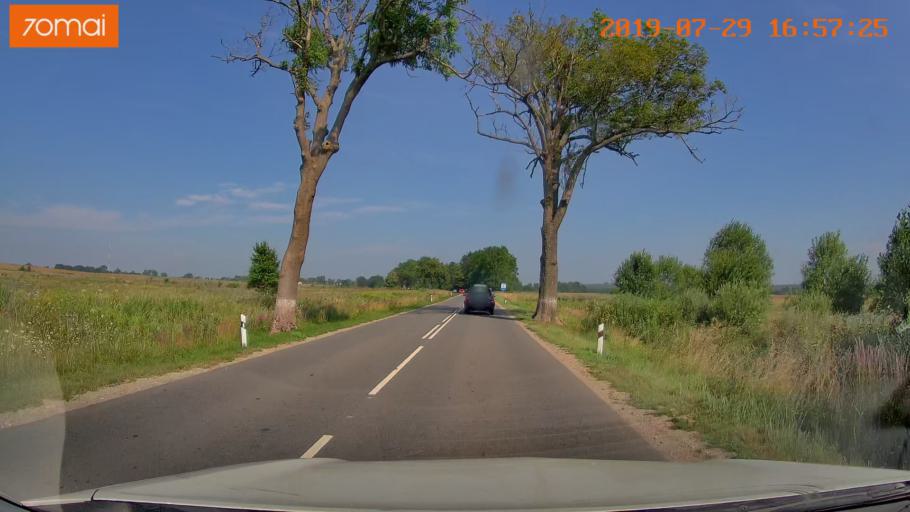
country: RU
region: Kaliningrad
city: Volochayevskoye
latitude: 54.8146
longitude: 20.1863
